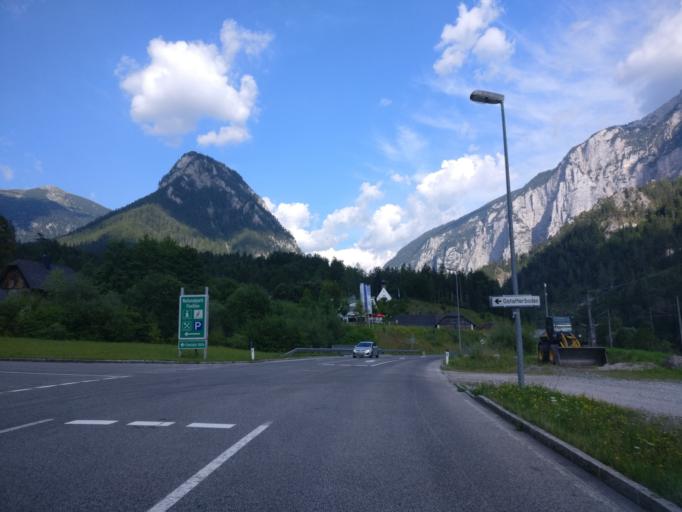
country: AT
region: Styria
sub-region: Politischer Bezirk Liezen
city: Johnsbach
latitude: 47.5916
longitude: 14.6346
